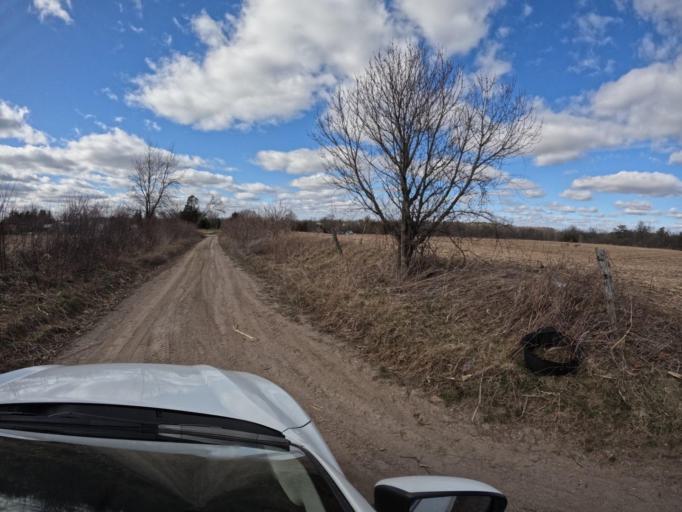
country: CA
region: Ontario
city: Norfolk County
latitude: 42.7615
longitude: -80.3169
